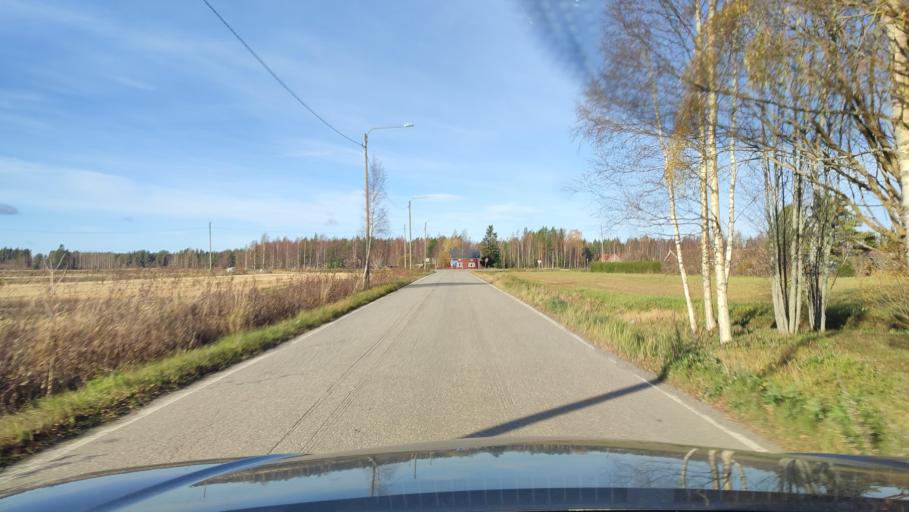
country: FI
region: Southern Ostrobothnia
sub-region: Suupohja
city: Teuva
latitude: 62.4506
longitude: 21.6029
